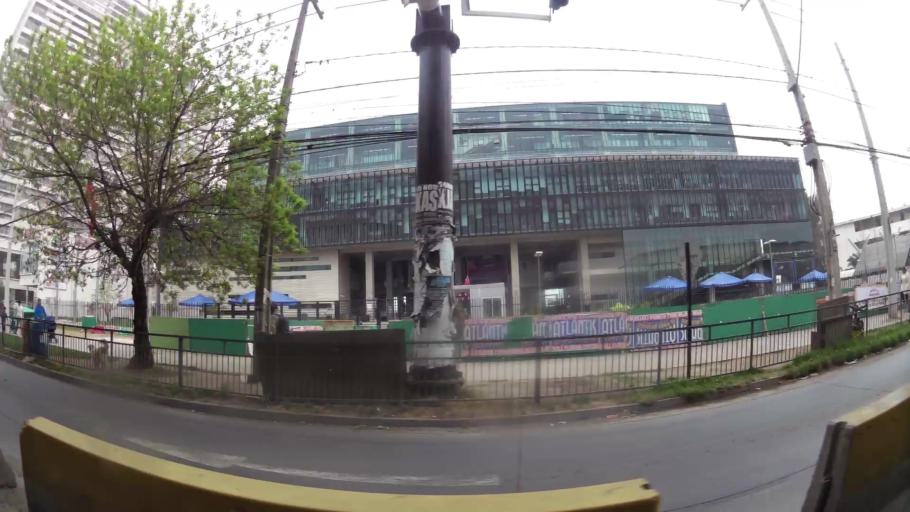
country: CL
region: Santiago Metropolitan
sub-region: Provincia de Santiago
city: Villa Presidente Frei, Nunoa, Santiago, Chile
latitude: -33.4998
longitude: -70.6158
